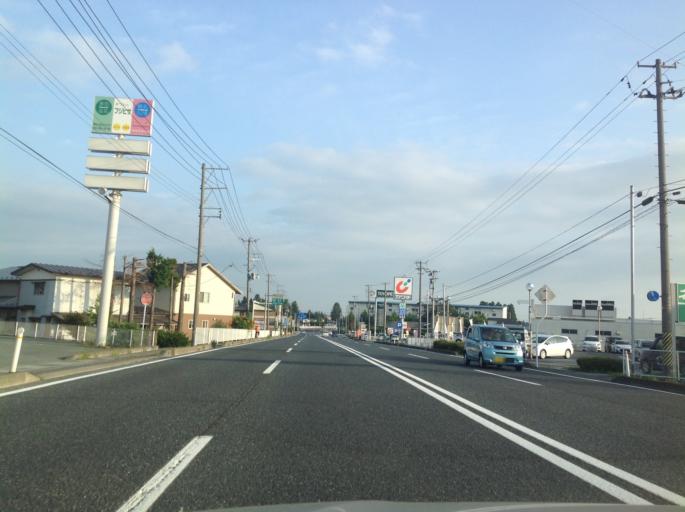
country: JP
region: Iwate
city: Morioka-shi
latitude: 39.5442
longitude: 141.1687
